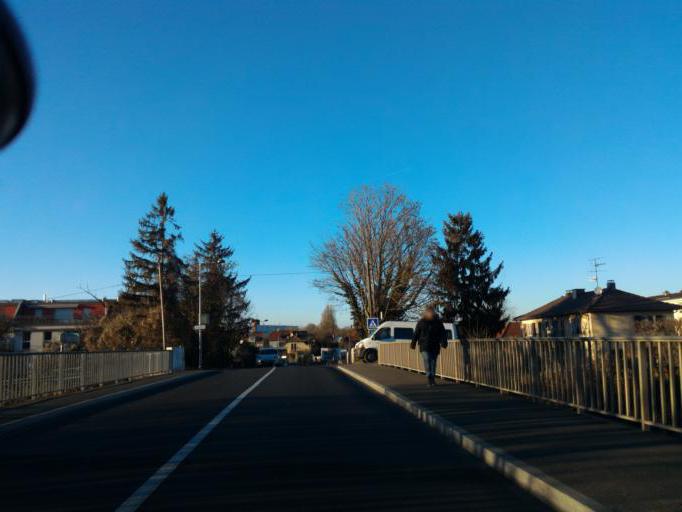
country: FR
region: Alsace
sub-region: Departement du Haut-Rhin
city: Riedisheim
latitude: 47.7564
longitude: 7.3676
